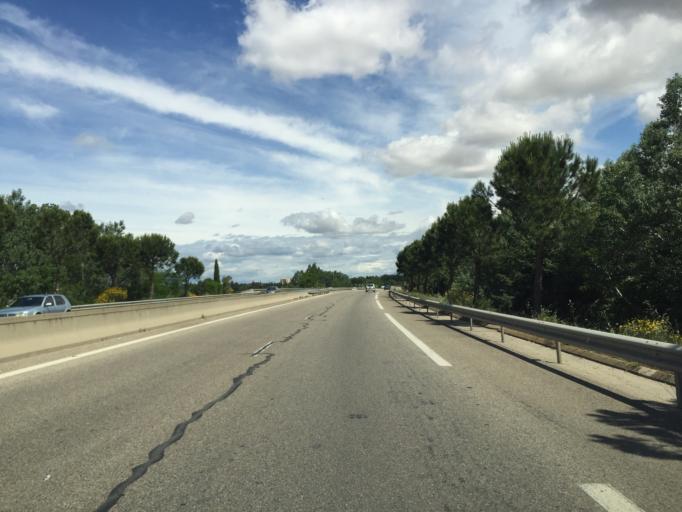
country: FR
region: Provence-Alpes-Cote d'Azur
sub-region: Departement du Vaucluse
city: Sorgues
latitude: 44.0039
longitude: 4.8638
